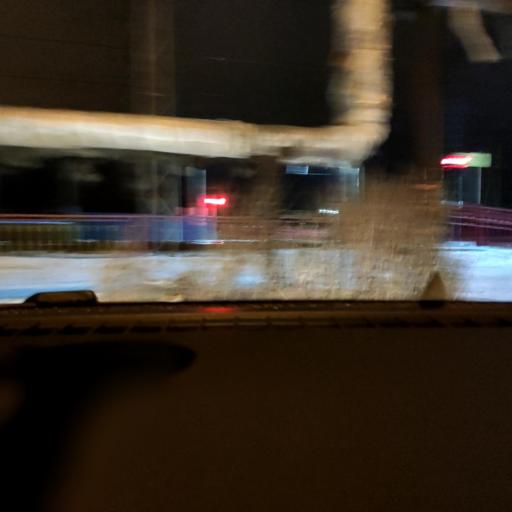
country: RU
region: Samara
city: Samara
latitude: 53.1844
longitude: 50.2139
